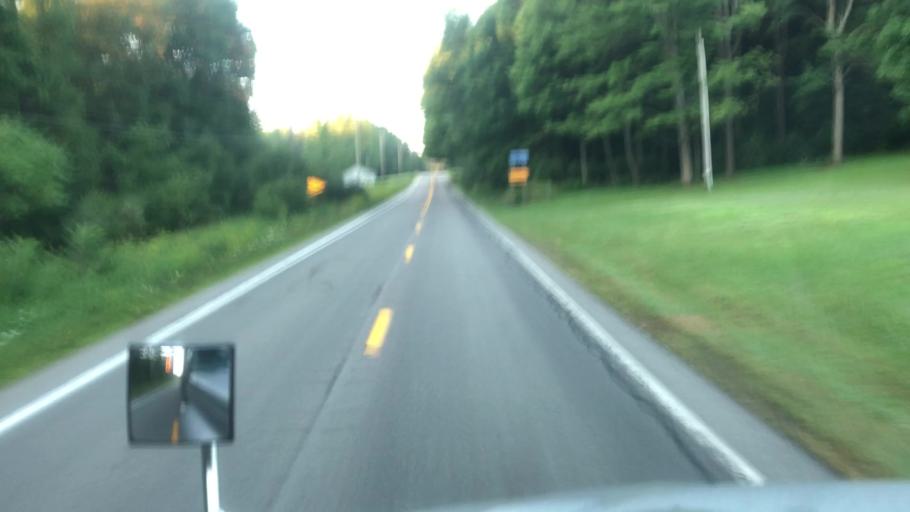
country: US
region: Pennsylvania
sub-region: Crawford County
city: Titusville
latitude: 41.5838
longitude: -79.6098
